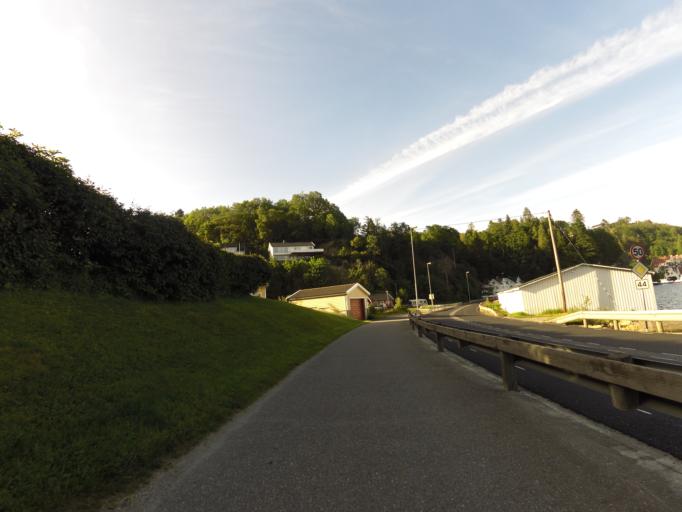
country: NO
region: Vest-Agder
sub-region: Flekkefjord
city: Flekkefjord
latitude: 58.2946
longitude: 6.6467
